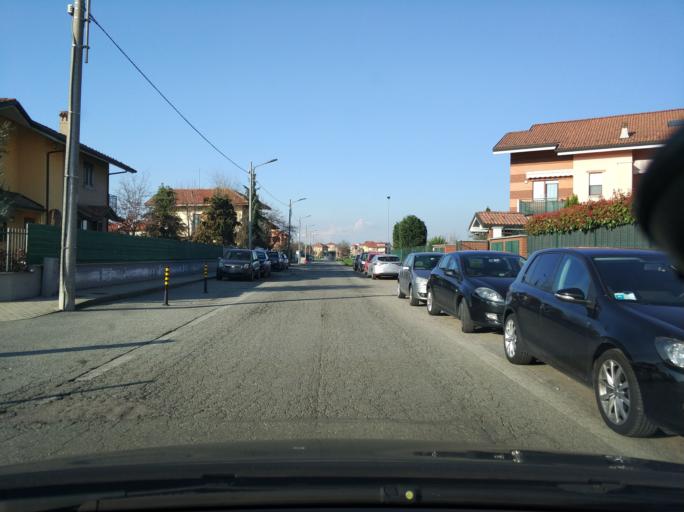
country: IT
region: Piedmont
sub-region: Provincia di Torino
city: San Maurizio
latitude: 45.1958
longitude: 7.6168
